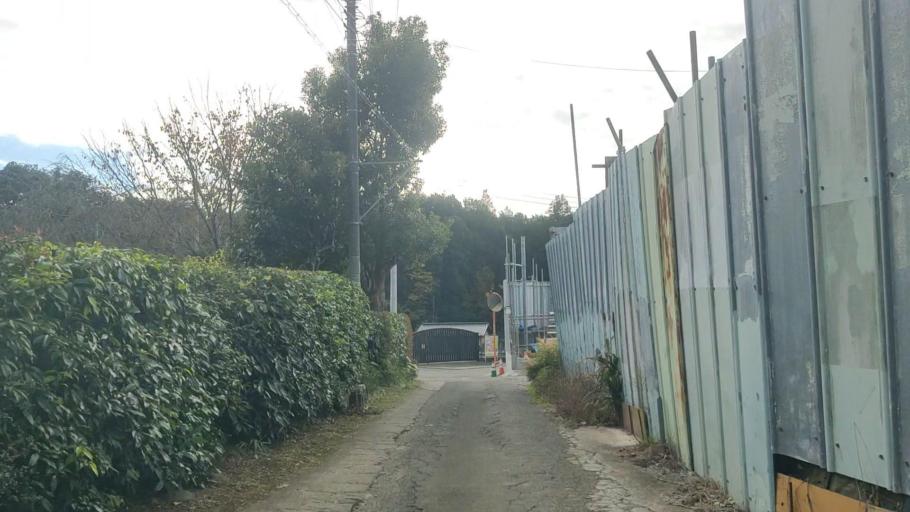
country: JP
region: Kanagawa
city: Minami-rinkan
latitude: 35.4924
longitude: 139.4955
